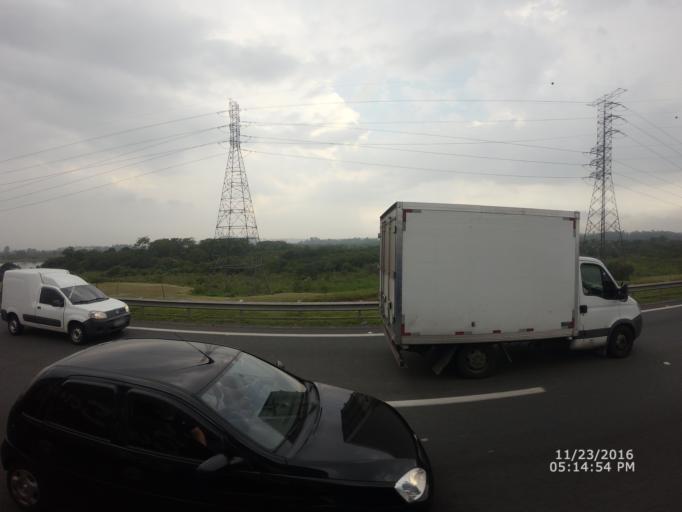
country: BR
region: Sao Paulo
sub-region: Guarulhos
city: Guarulhos
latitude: -23.4772
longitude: -46.5167
